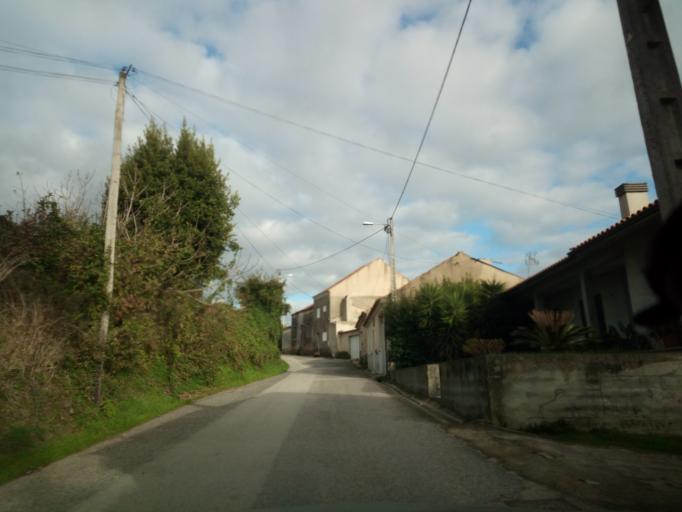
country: PT
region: Aveiro
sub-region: Oliveira do Bairro
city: Oliveira do Bairro
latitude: 40.5416
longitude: -8.4902
